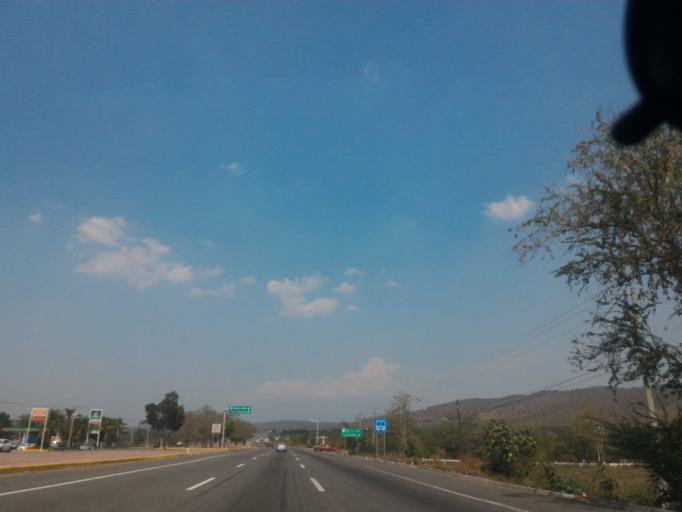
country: MX
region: Colima
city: Coquimatlan
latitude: 19.1388
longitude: -103.7716
